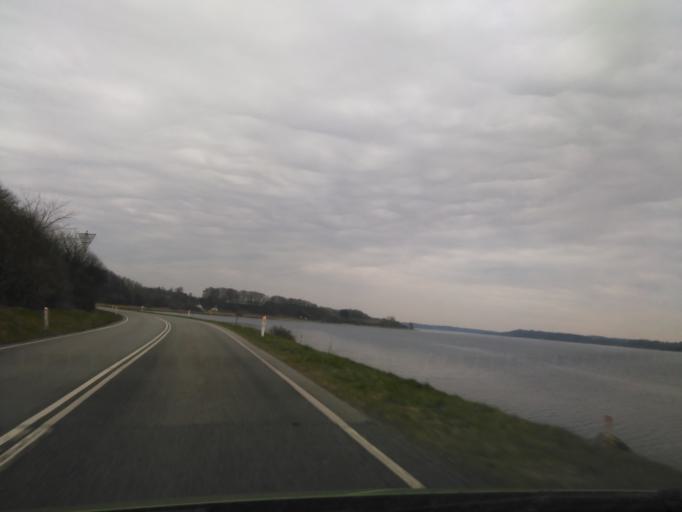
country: DK
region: North Denmark
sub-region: Mariagerfjord Kommune
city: Mariager
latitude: 56.6688
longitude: 10.0059
